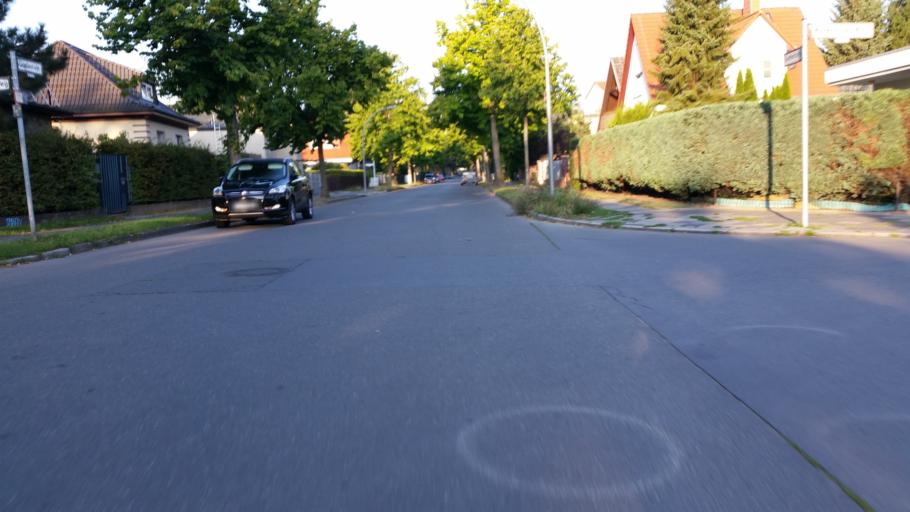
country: DE
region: Berlin
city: Lichtenrade
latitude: 52.4039
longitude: 13.4033
